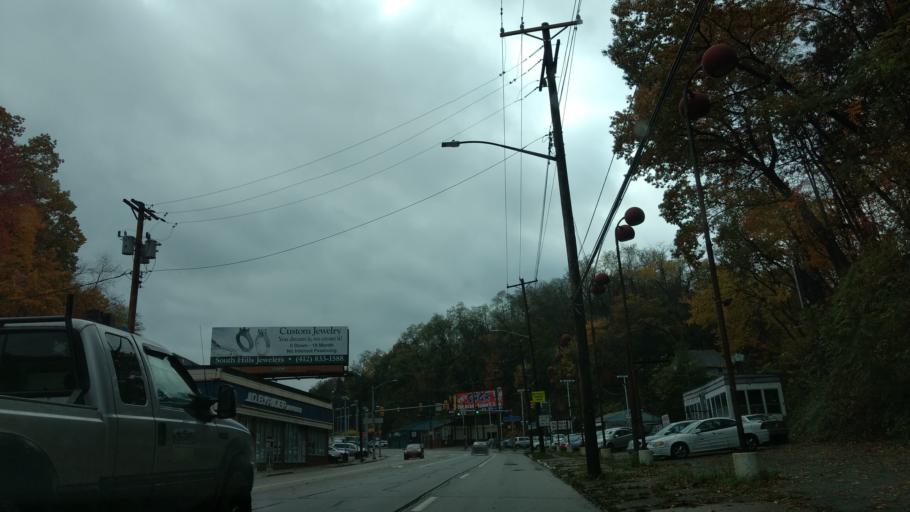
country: US
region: Pennsylvania
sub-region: Allegheny County
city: Dormont
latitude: 40.4091
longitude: -80.0170
